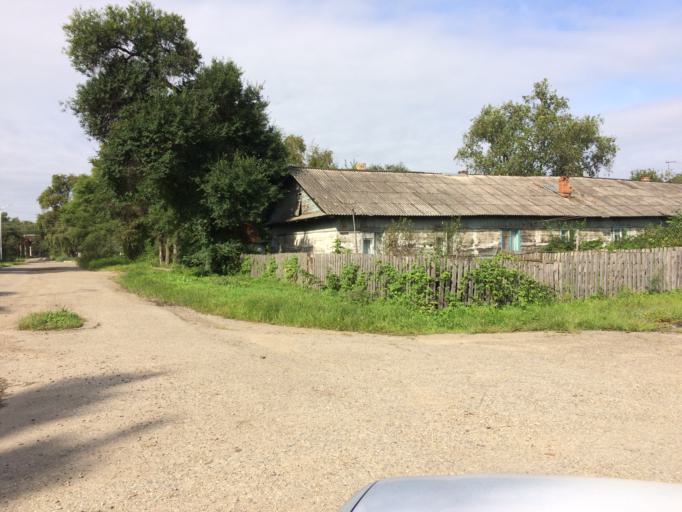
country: RU
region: Primorskiy
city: Dal'nerechensk
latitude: 45.9360
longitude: 133.7458
